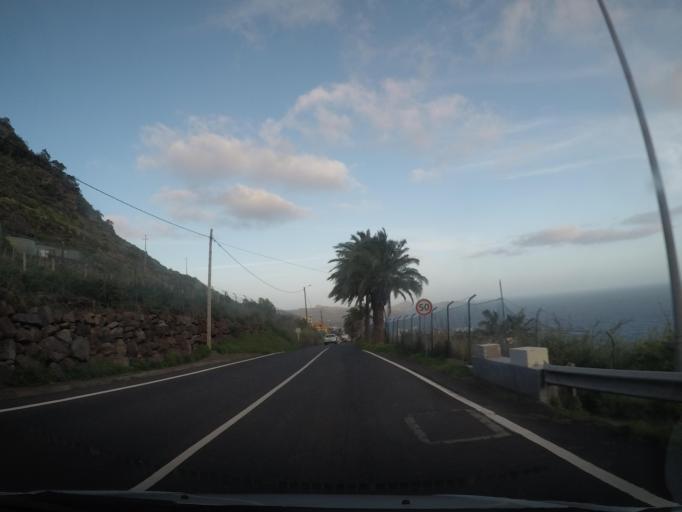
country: PT
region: Madeira
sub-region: Machico
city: Canical
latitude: 32.7382
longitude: -16.7501
